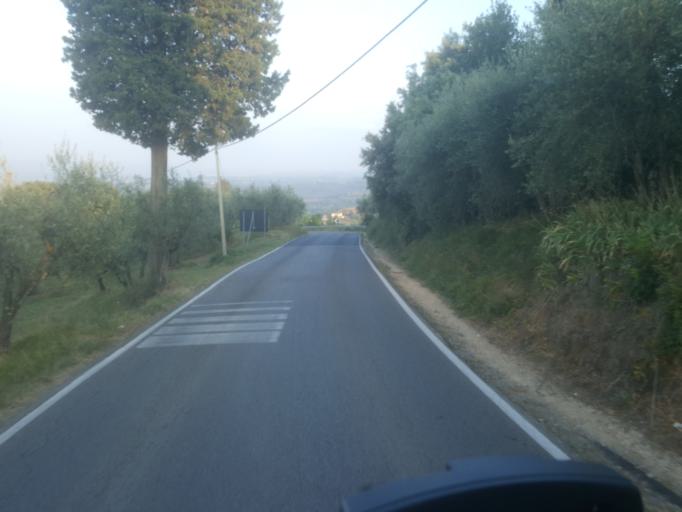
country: IT
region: Tuscany
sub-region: Province of Florence
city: Gambassi Terme
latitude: 43.5411
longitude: 10.9575
